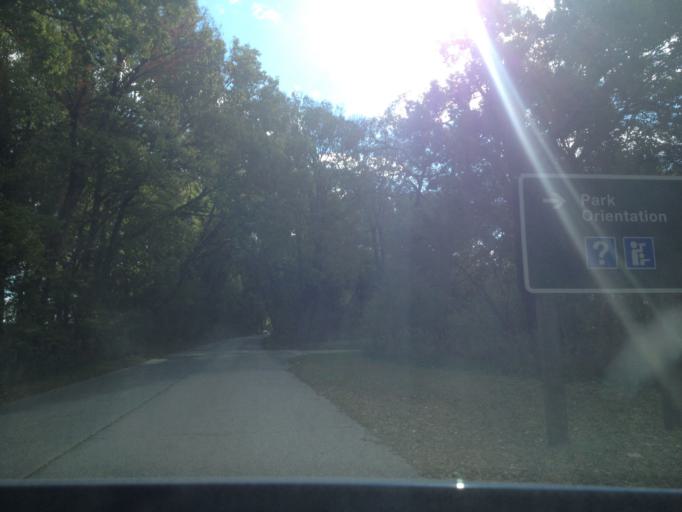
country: CA
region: Ontario
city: Amherstburg
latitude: 41.9834
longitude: -82.5457
